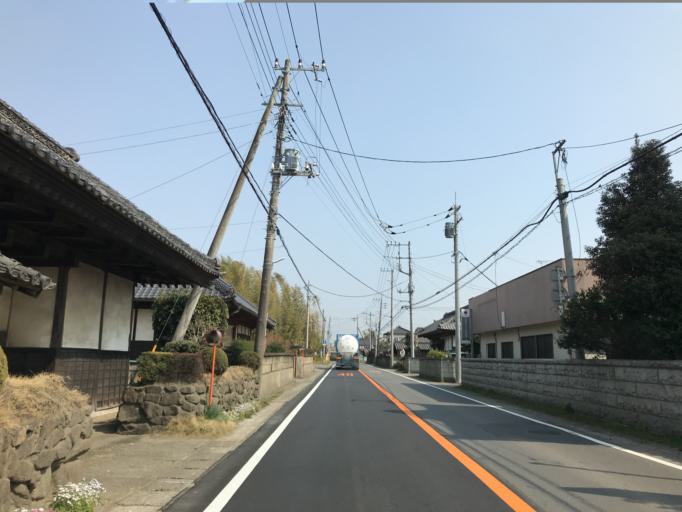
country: JP
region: Ibaraki
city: Tsukuba
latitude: 36.1485
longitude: 140.1567
